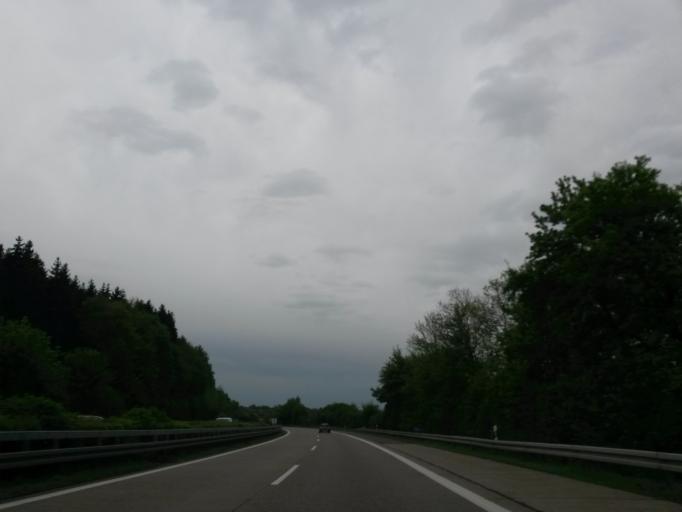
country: DE
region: Baden-Wuerttemberg
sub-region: Regierungsbezirk Stuttgart
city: Eberstadt
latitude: 49.1976
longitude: 9.3501
